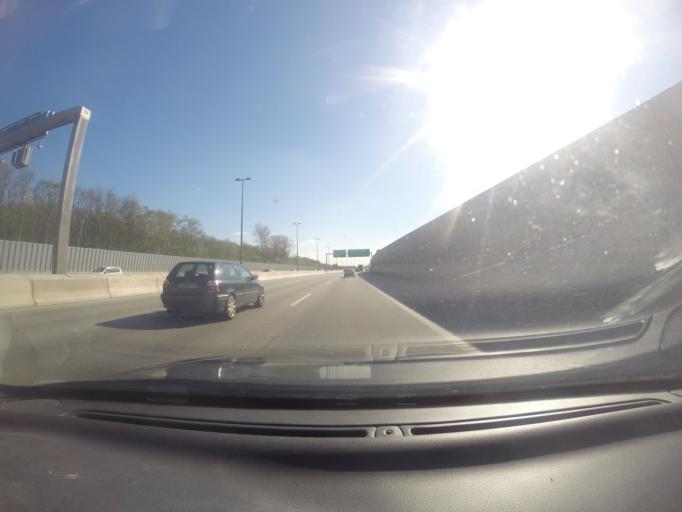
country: DK
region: Capital Region
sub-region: Rodovre Kommune
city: Rodovre
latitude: 55.6998
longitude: 12.4459
